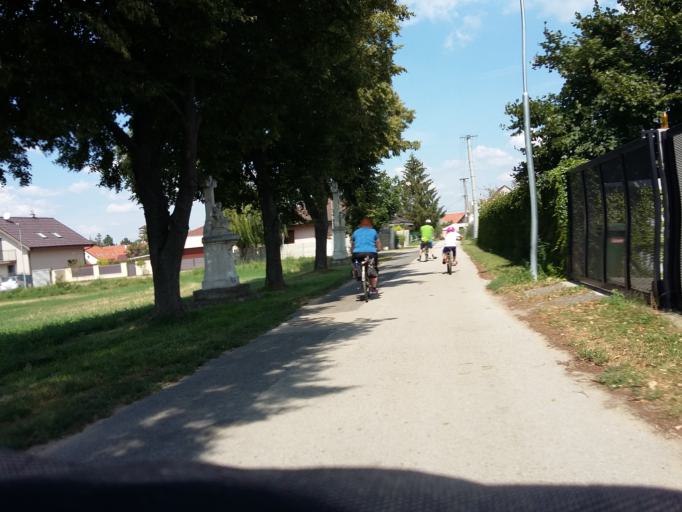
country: SK
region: Bratislavsky
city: Stupava
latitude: 48.3302
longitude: 17.0420
